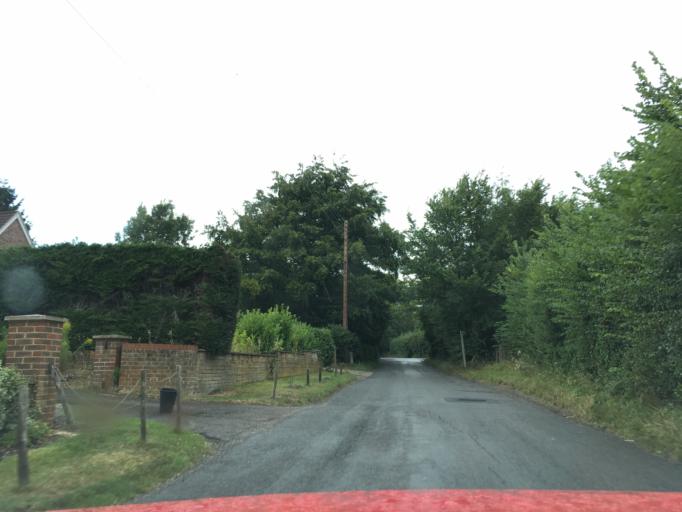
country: GB
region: England
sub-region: Kent
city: Marden
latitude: 51.2176
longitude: 0.4758
